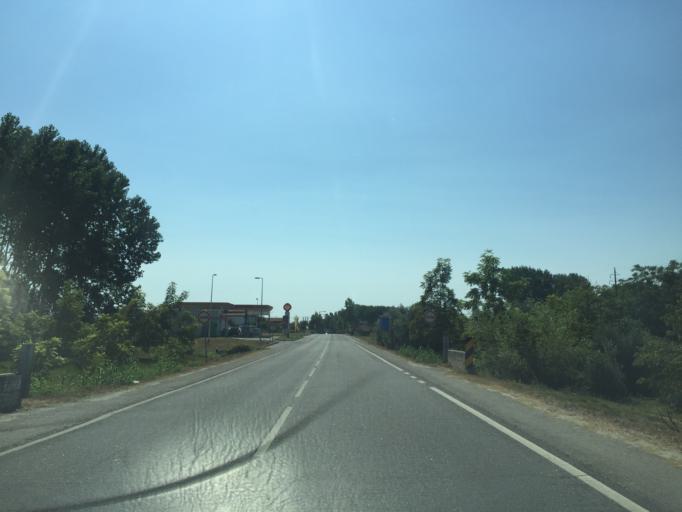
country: PT
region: Coimbra
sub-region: Cantanhede
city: Cantanhede
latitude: 40.3511
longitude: -8.5781
